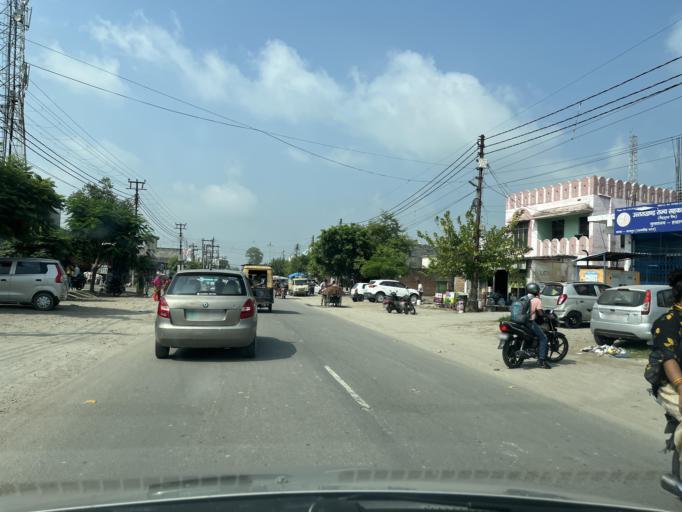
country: IN
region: Uttarakhand
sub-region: Udham Singh Nagar
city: Bazpur
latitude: 29.1544
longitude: 79.1455
